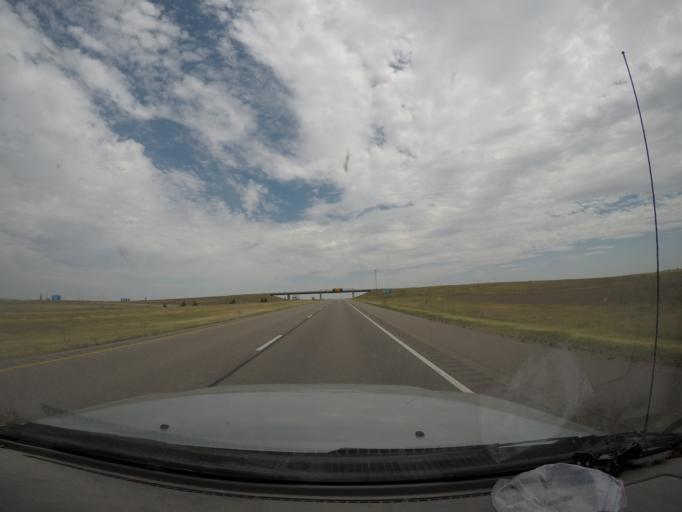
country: US
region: Nebraska
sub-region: Kimball County
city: Kimball
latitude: 41.2044
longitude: -103.7232
